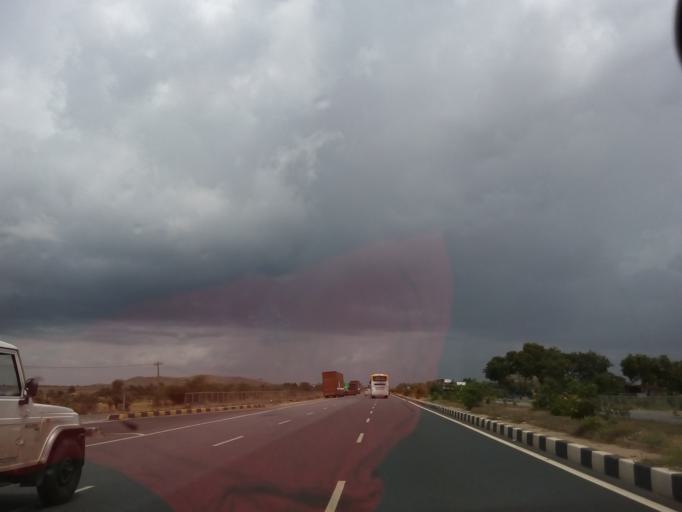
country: IN
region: Karnataka
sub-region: Chitradurga
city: Chitradurga
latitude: 14.1664
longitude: 76.4752
